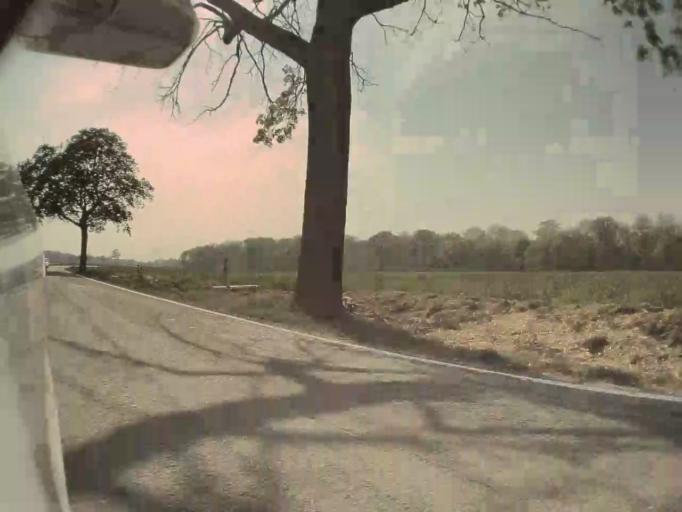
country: BE
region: Wallonia
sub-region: Province de Namur
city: Hamois
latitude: 50.3064
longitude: 5.2260
